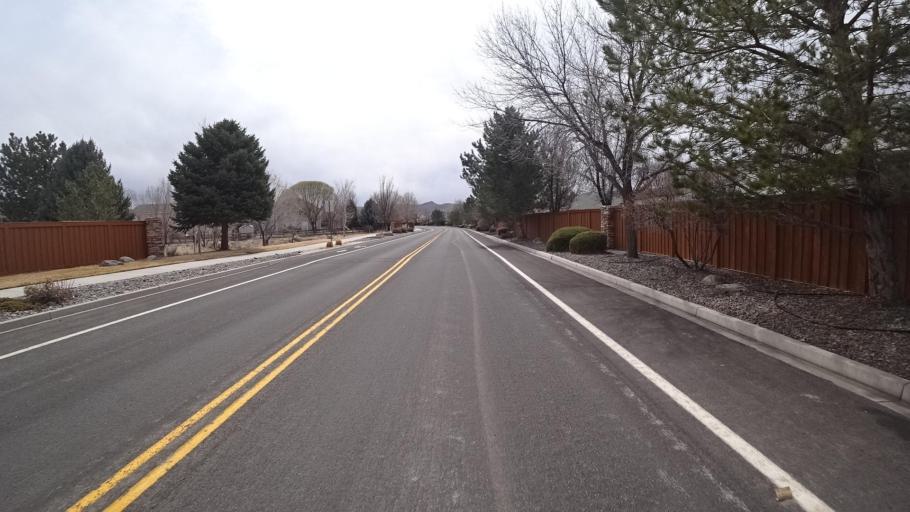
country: US
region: Nevada
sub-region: Washoe County
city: Spanish Springs
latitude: 39.6283
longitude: -119.6843
